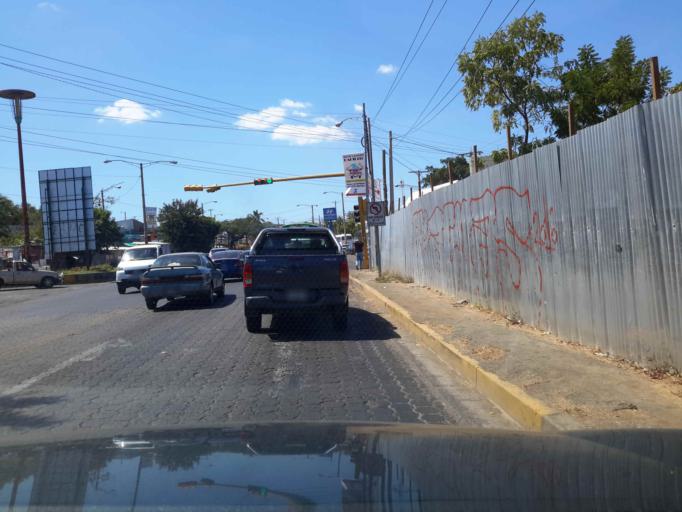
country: NI
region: Managua
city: Managua
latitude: 12.1481
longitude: -86.2868
